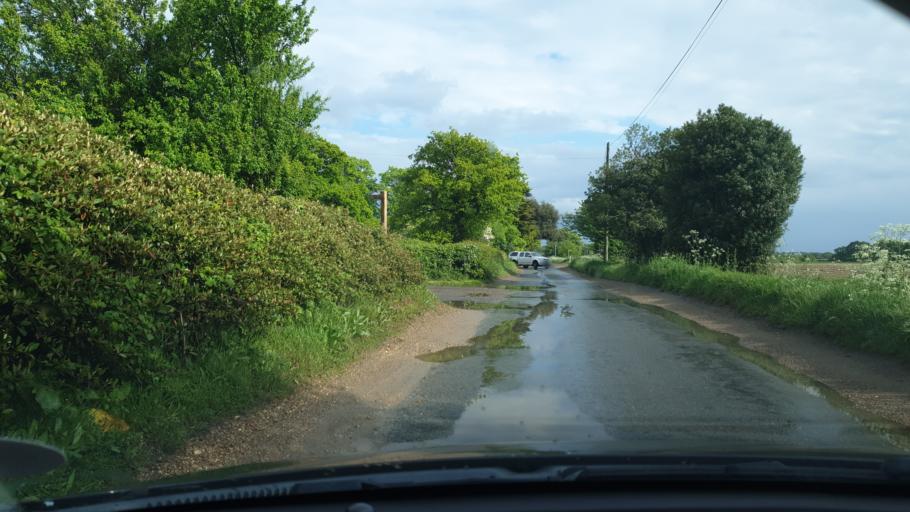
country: GB
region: England
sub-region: Essex
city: Great Bentley
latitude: 51.8465
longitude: 1.0473
